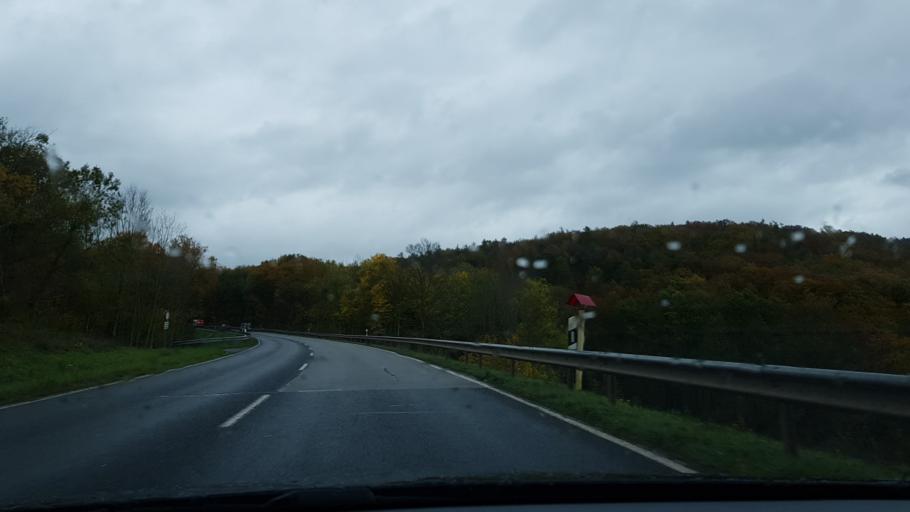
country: DE
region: Rheinland-Pfalz
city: Salmtal
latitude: 49.9394
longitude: 6.8508
